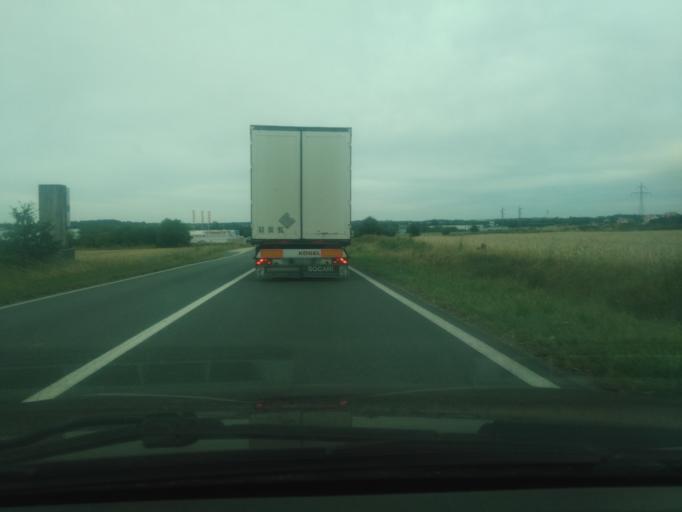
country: FR
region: Poitou-Charentes
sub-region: Departement de la Vienne
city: Chauvigny
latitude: 46.5669
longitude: 0.6141
